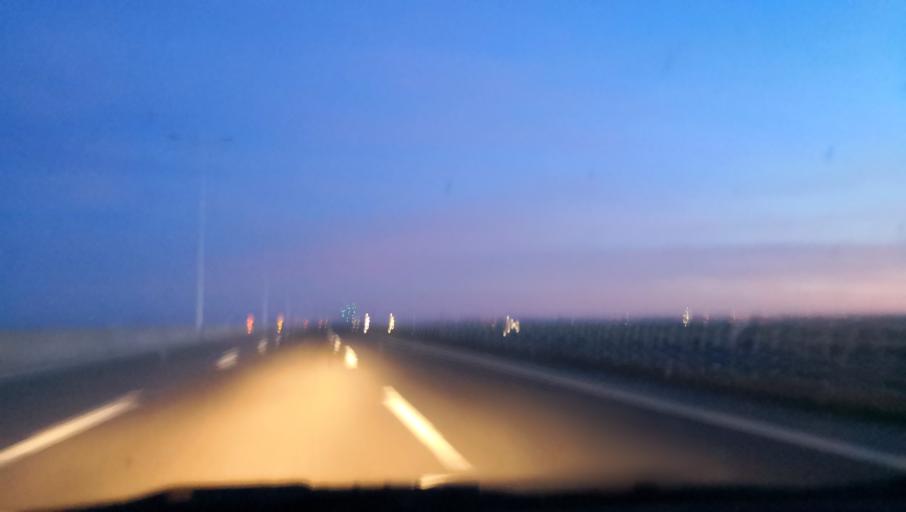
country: PT
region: Lisbon
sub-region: Vila Franca de Xira
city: Castanheira do Ribatejo
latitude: 38.9995
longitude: -8.9038
